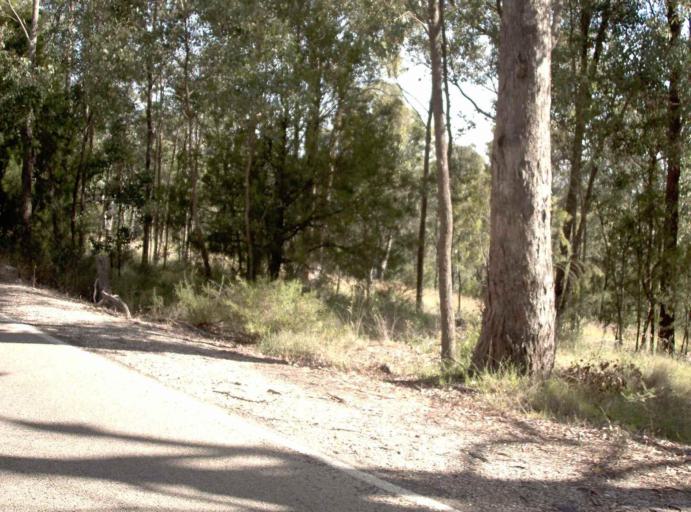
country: AU
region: Victoria
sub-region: East Gippsland
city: Lakes Entrance
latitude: -37.7754
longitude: 147.8185
